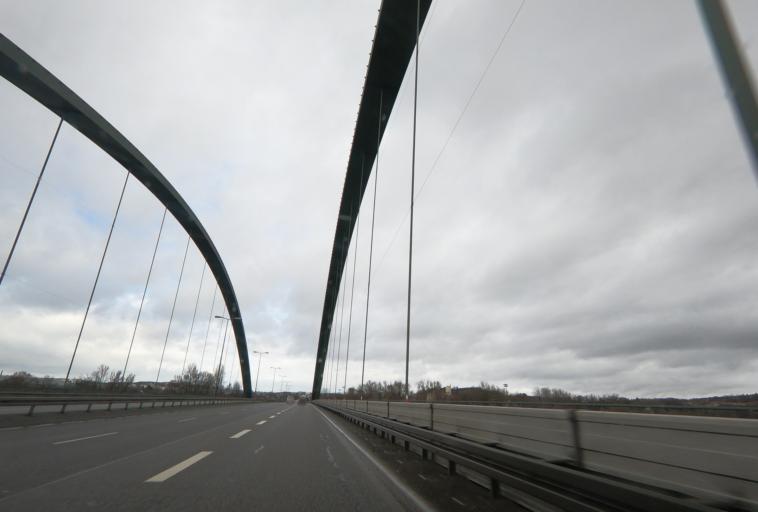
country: DE
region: Bavaria
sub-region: Upper Palatinate
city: Regensburg
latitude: 49.0225
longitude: 12.1414
